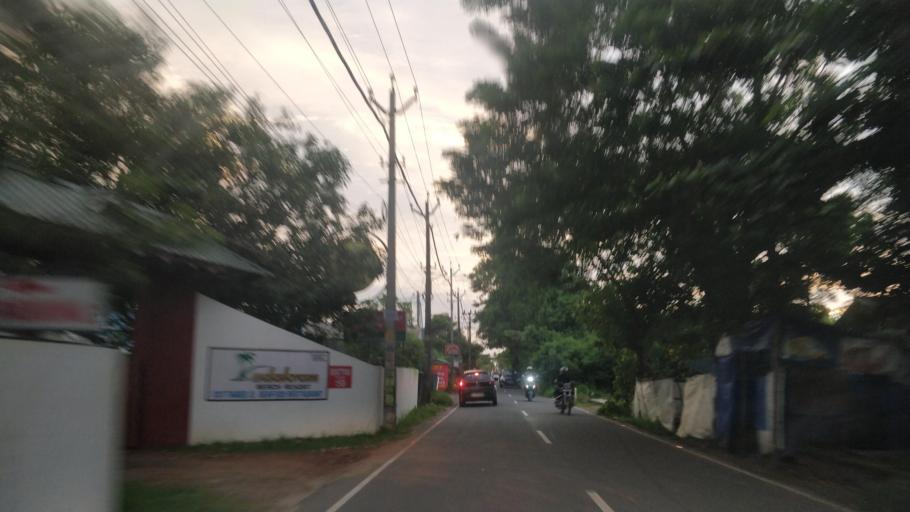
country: IN
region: Kerala
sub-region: Thrissur District
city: Kodungallur
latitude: 10.1400
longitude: 76.1857
